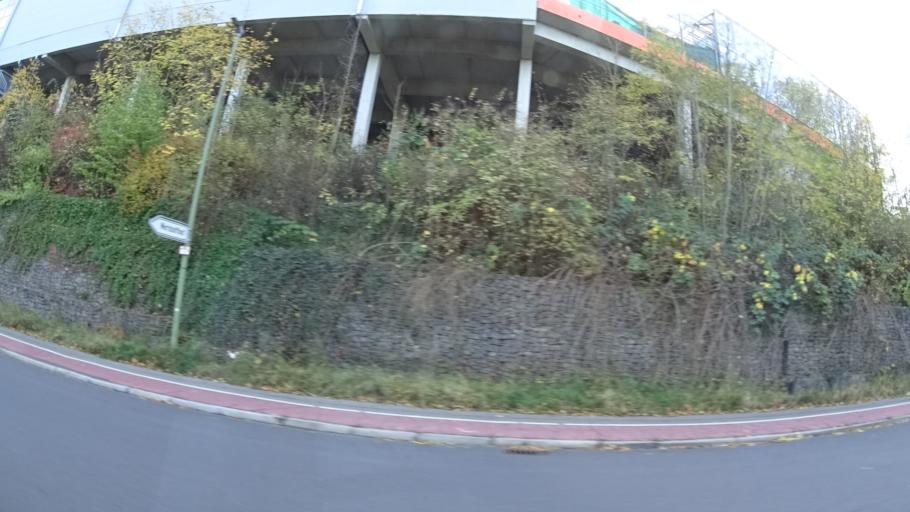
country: DE
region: Baden-Wuerttemberg
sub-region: Regierungsbezirk Stuttgart
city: Leonberg
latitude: 48.7986
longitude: 9.0018
